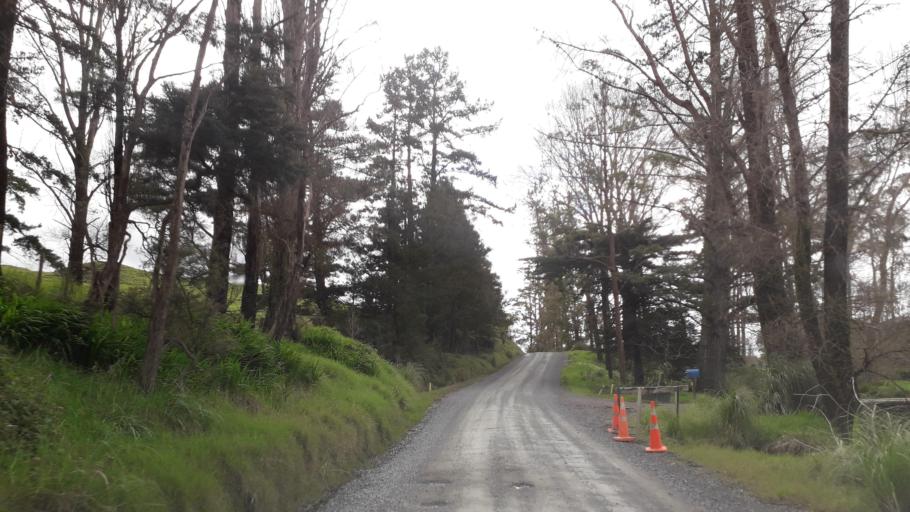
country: NZ
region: Northland
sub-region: Far North District
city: Taipa
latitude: -35.0922
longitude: 173.5157
